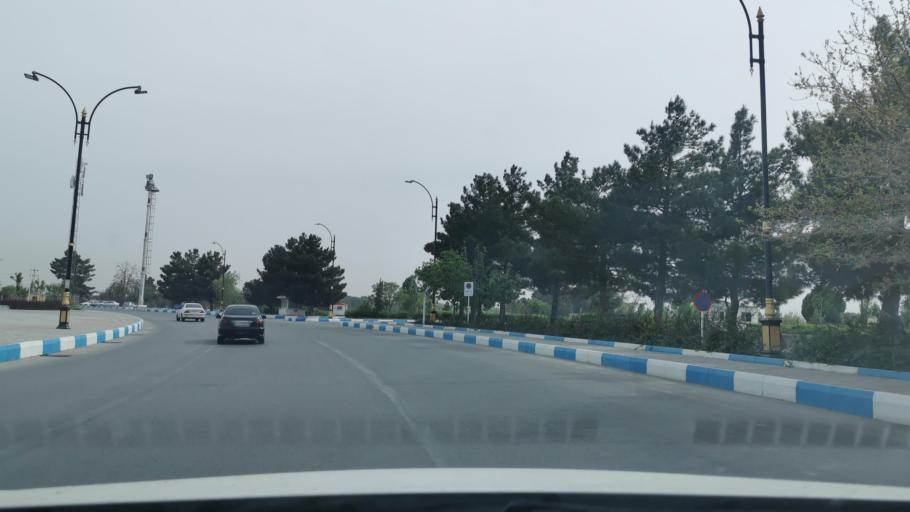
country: IR
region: Razavi Khorasan
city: Mashhad
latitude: 36.2269
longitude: 59.6391
